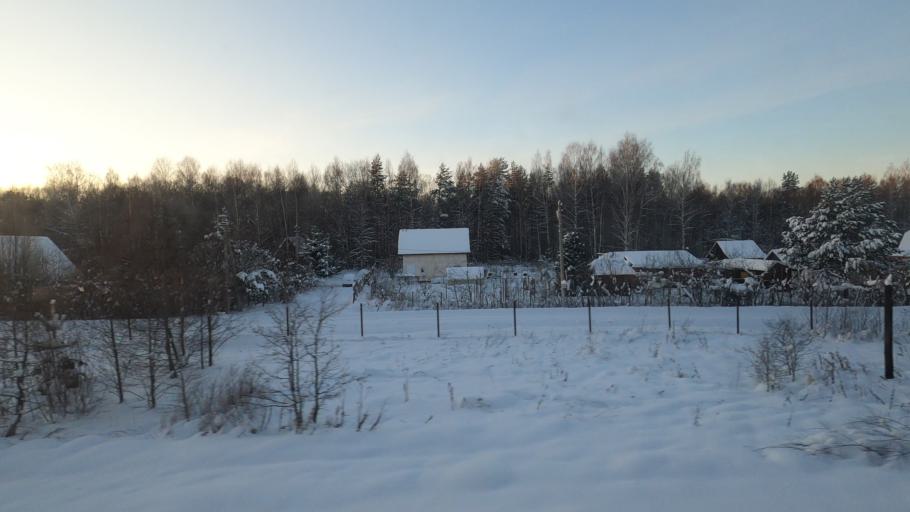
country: RU
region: Moskovskaya
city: Orud'yevo
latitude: 56.4275
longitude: 37.4986
